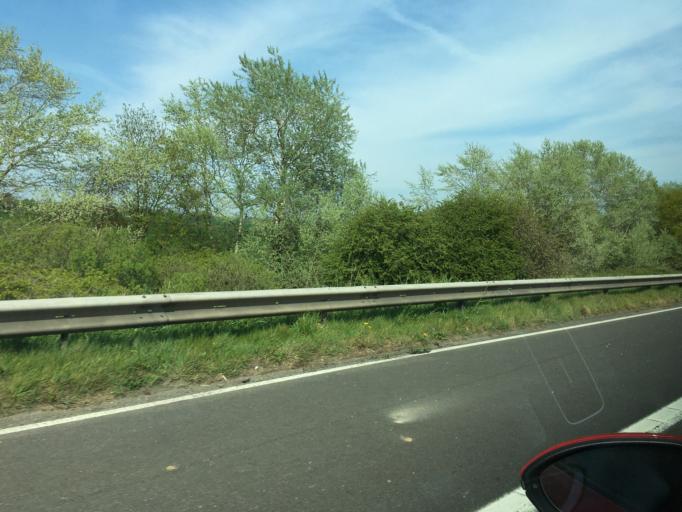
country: GB
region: England
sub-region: South Gloucestershire
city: Hinton
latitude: 51.4980
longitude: -2.3968
